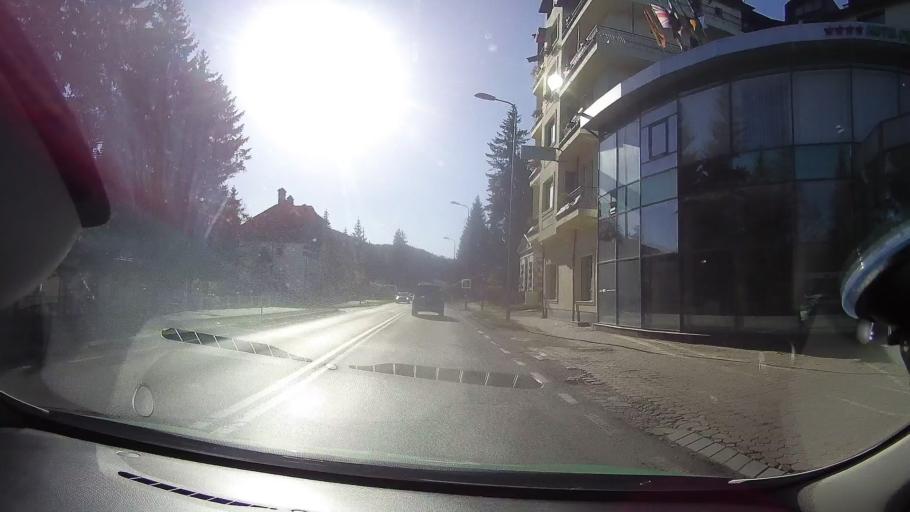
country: RO
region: Brasov
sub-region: Oras Predeal
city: Predeal
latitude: 45.5103
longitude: 25.5736
